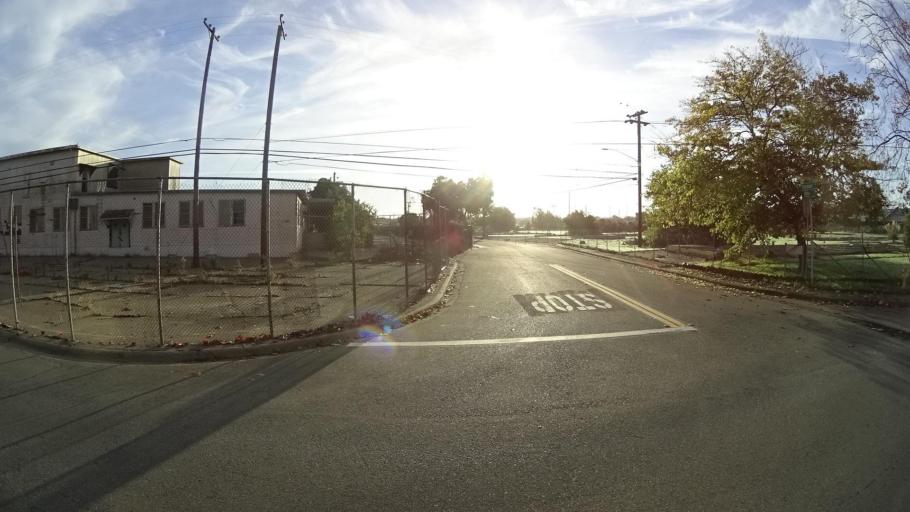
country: US
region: California
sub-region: Alameda County
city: Oakland
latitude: 37.7842
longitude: -122.2938
